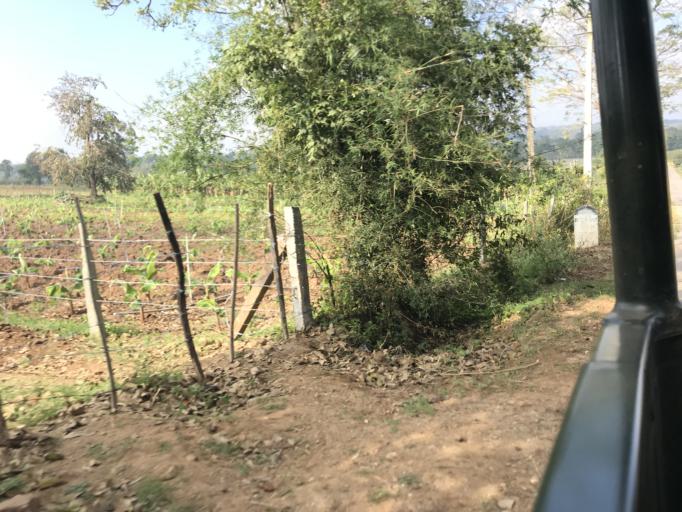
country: IN
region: Karnataka
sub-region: Mysore
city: Heggadadevankote
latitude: 11.9469
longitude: 76.2522
